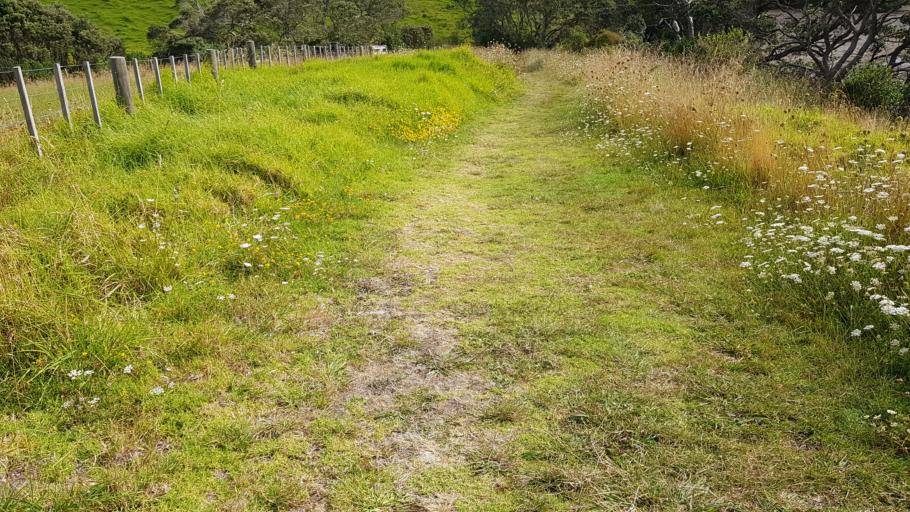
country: NZ
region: Auckland
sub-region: Auckland
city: Rothesay Bay
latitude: -36.6631
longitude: 174.7407
